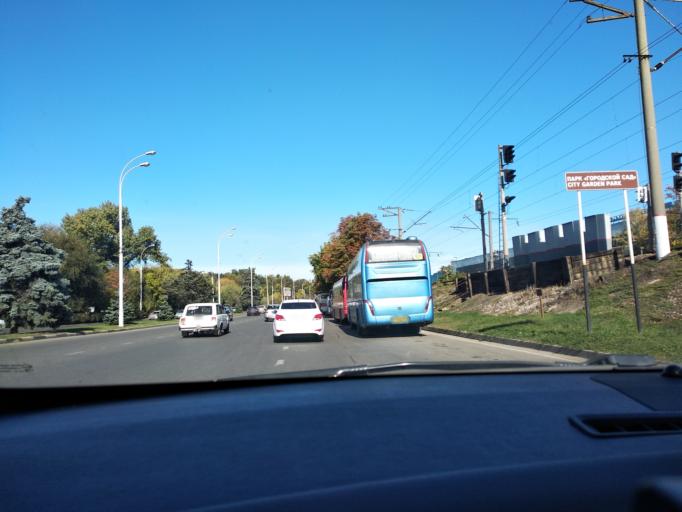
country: RU
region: Adygeya
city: Yablonovskiy
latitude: 45.0076
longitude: 38.9686
